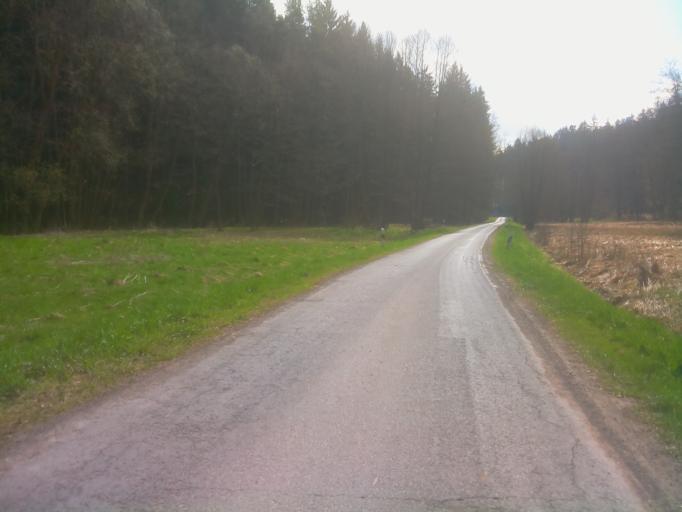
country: DE
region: Thuringia
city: Trockenborn-Wolfersdorf
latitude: 50.7870
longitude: 11.7137
